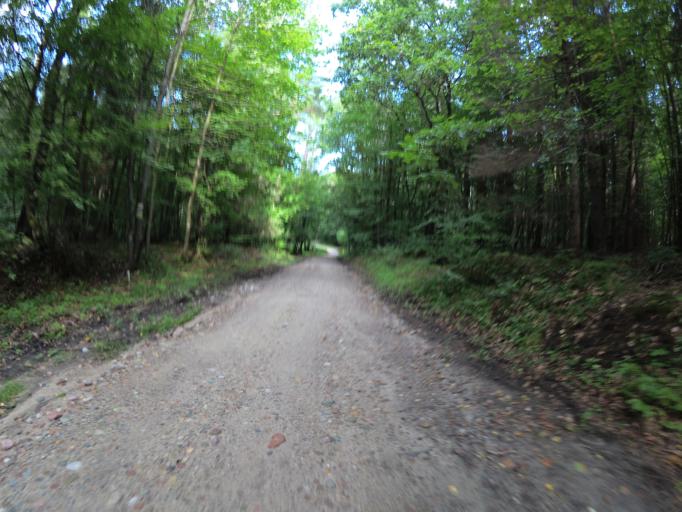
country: PL
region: Pomeranian Voivodeship
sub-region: Gdynia
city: Wielki Kack
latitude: 54.4913
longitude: 18.4728
